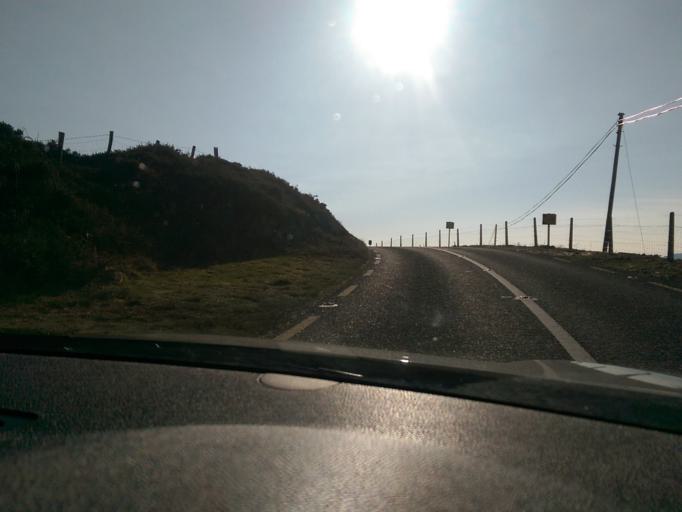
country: IE
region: Connaught
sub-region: County Galway
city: Clifden
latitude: 53.3882
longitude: -9.7881
